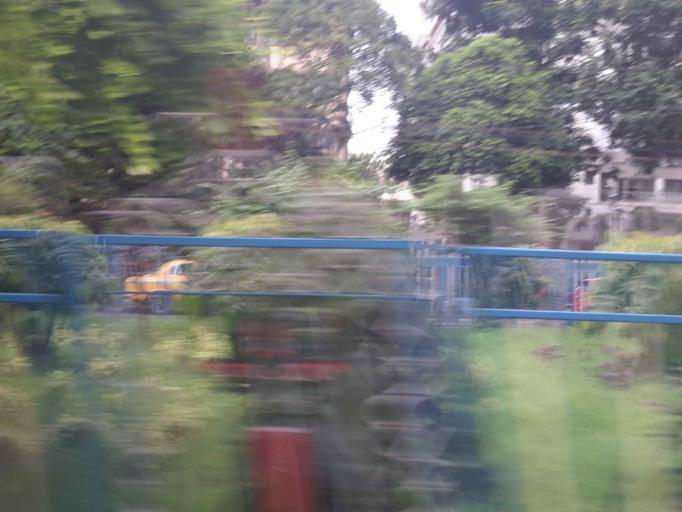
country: IN
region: West Bengal
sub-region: Kolkata
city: Kolkata
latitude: 22.5134
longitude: 88.3567
